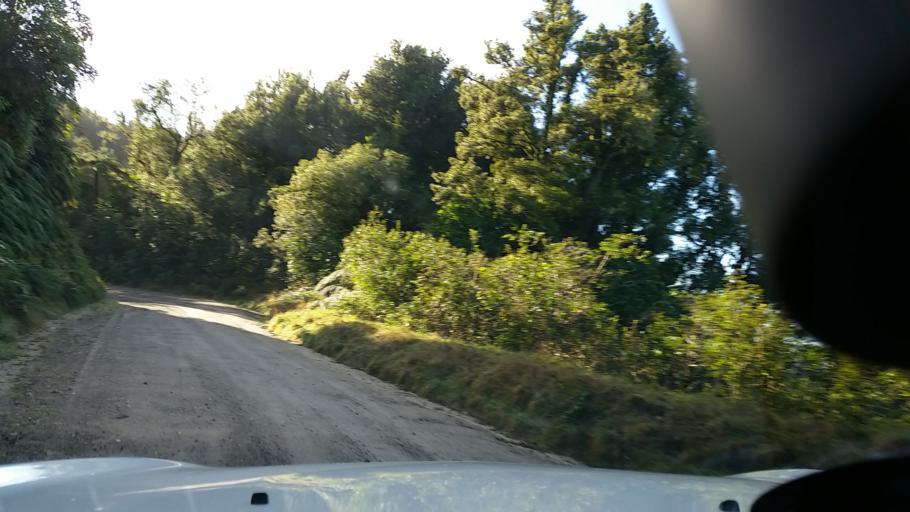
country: NZ
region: Bay of Plenty
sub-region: Kawerau District
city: Kawerau
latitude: -38.0199
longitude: 176.5822
